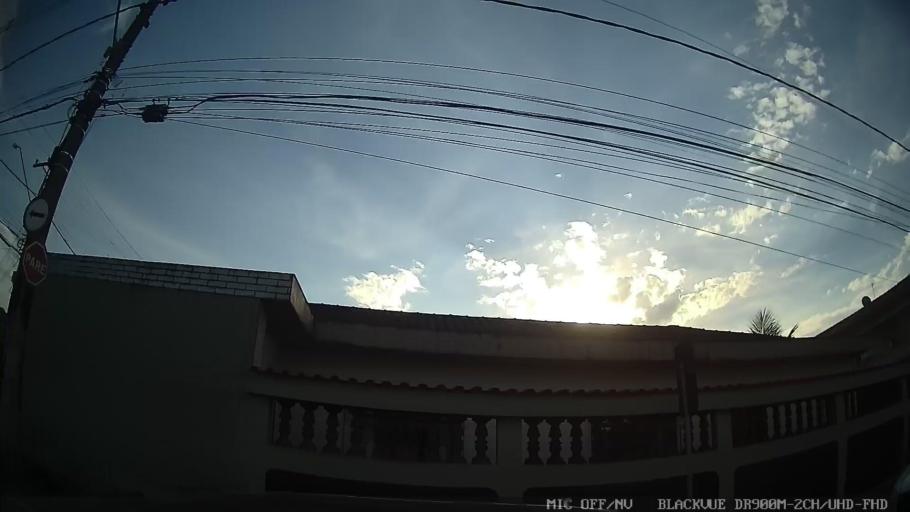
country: BR
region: Sao Paulo
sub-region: Cubatao
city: Cubatao
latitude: -23.8992
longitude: -46.4258
